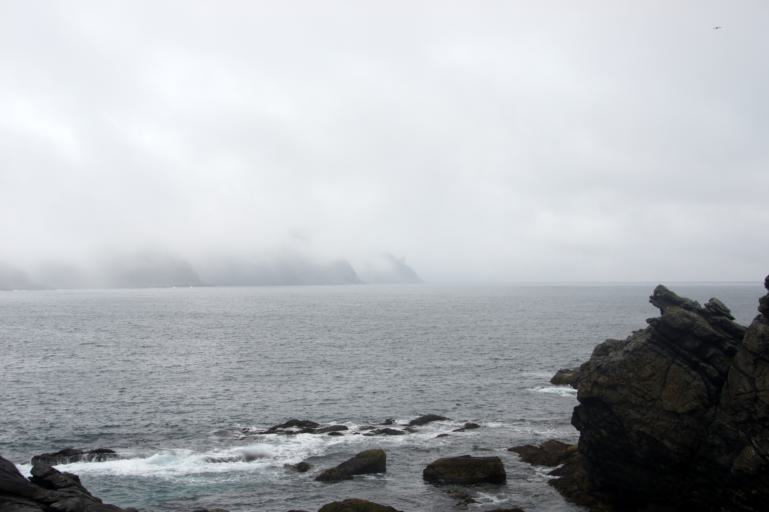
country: NO
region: Finnmark Fylke
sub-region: Nordkapp
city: Honningsvag
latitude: 71.1135
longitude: 25.8018
